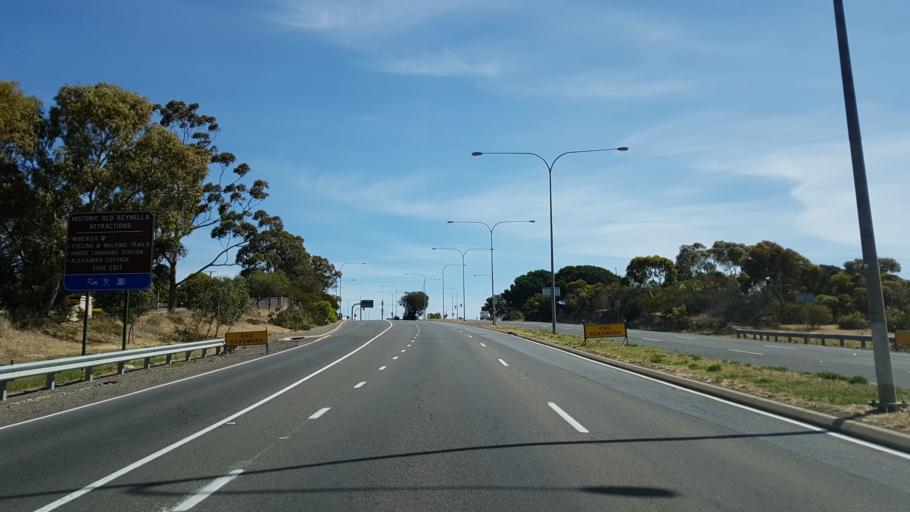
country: AU
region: South Australia
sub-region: Marion
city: Trott Park
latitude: -35.0788
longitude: 138.5479
